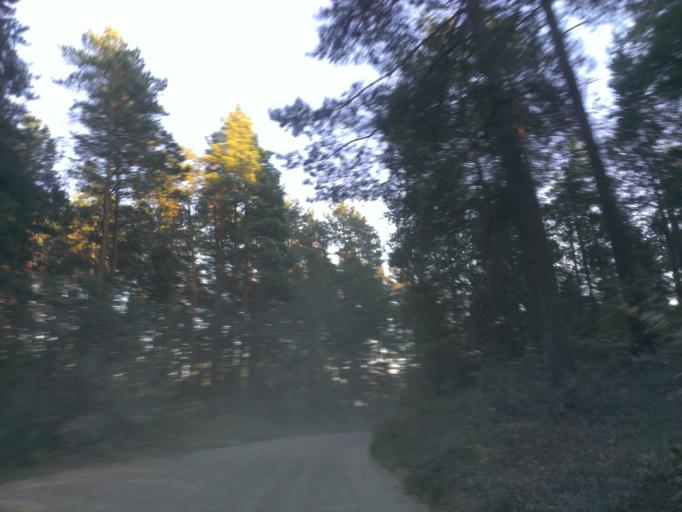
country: LV
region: Garkalne
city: Garkalne
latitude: 57.0511
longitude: 24.4177
